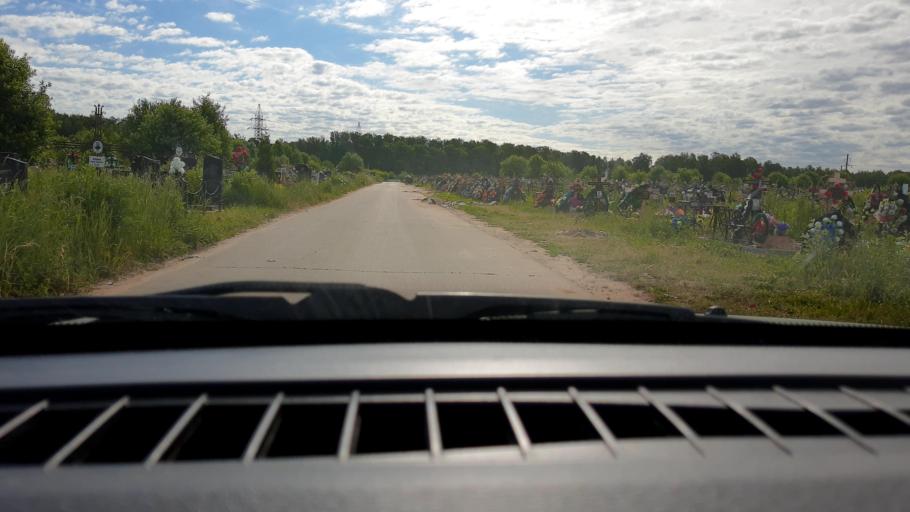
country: RU
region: Nizjnij Novgorod
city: Afonino
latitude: 56.2311
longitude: 44.0777
